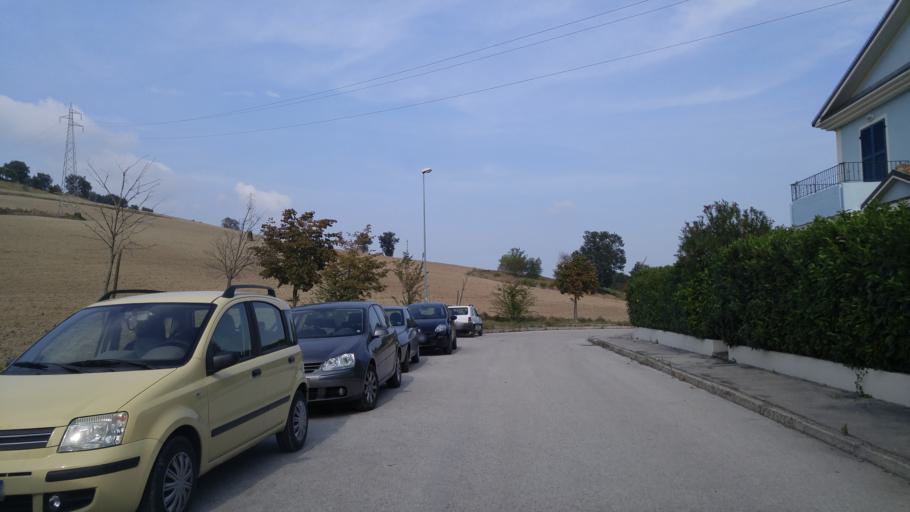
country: IT
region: The Marches
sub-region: Provincia di Pesaro e Urbino
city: Montefelcino
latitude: 43.7168
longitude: 12.8551
